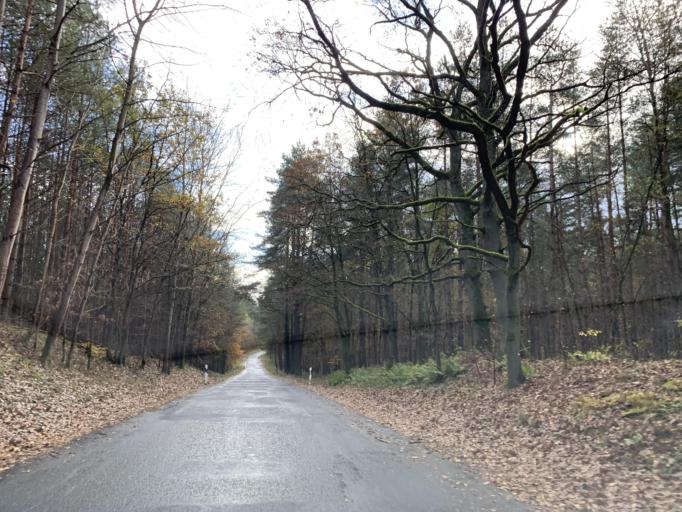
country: DE
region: Mecklenburg-Vorpommern
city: Blankensee
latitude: 53.3939
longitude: 13.2619
